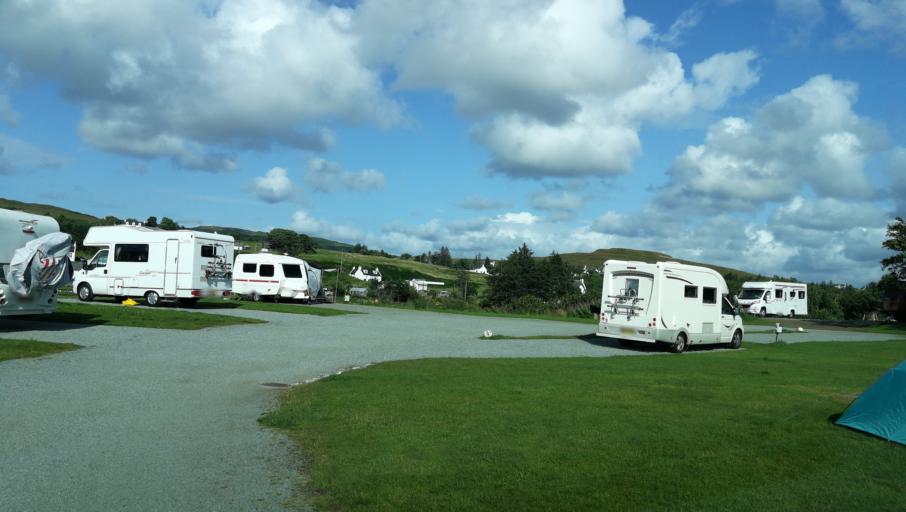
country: GB
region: Scotland
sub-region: Highland
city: Isle of Skye
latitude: 57.4320
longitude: -6.5799
